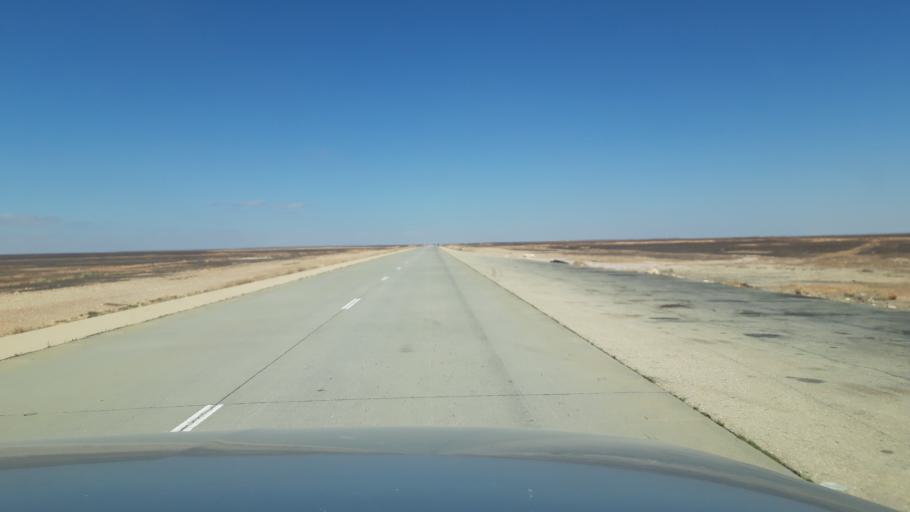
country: SA
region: Al Jawf
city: Al Qurayyat
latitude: 31.1856
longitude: 36.6643
